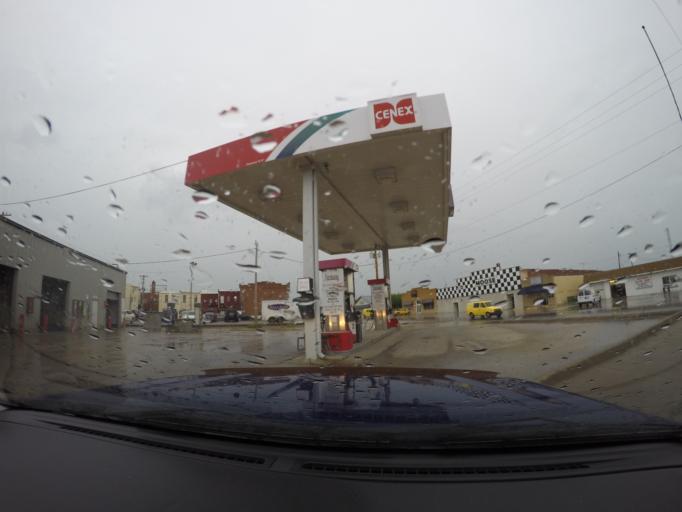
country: US
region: Kansas
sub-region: Cloud County
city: Concordia
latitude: 39.5724
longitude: -97.6595
